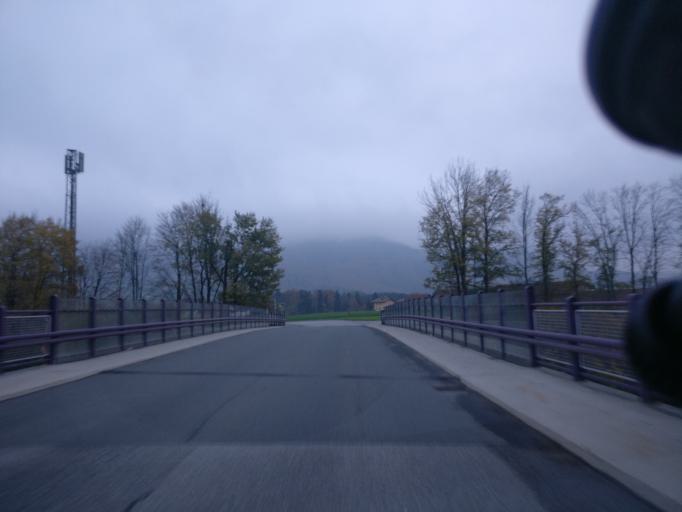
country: AT
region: Salzburg
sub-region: Politischer Bezirk Salzburg-Umgebung
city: Hallwang
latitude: 47.8511
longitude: 13.0885
